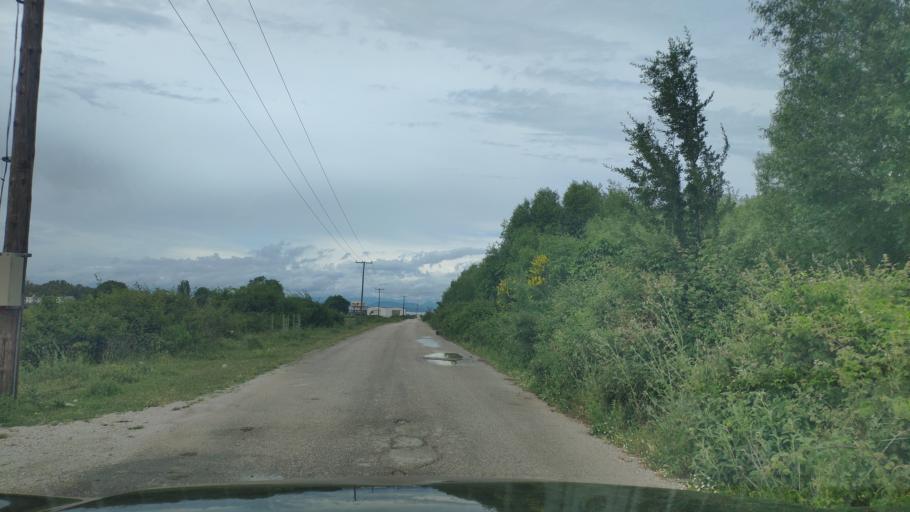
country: GR
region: West Greece
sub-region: Nomos Aitolias kai Akarnanias
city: Vonitsa
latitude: 38.9142
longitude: 20.9078
